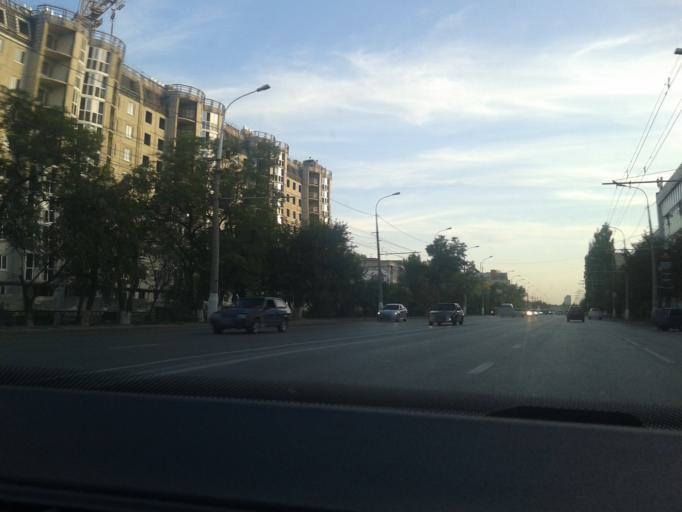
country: RU
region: Volgograd
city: Volgograd
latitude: 48.7334
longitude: 44.5425
